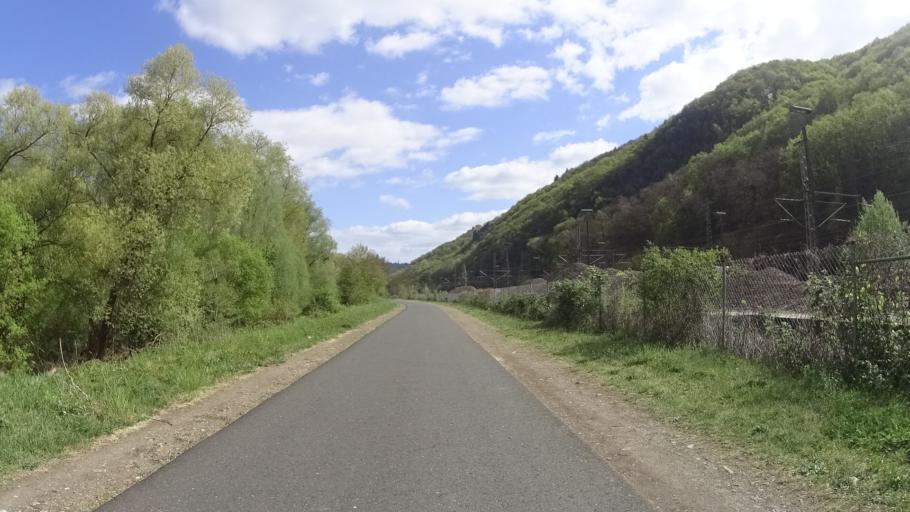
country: DE
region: Rheinland-Pfalz
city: Weiler
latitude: 49.9744
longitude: 7.8679
